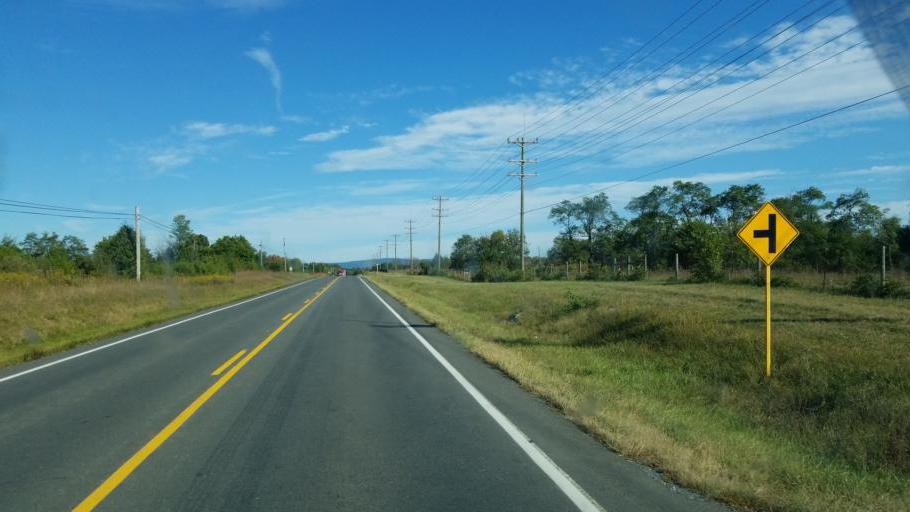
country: US
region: Virginia
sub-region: Frederick County
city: Stephens City
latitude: 39.0593
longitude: -78.1281
